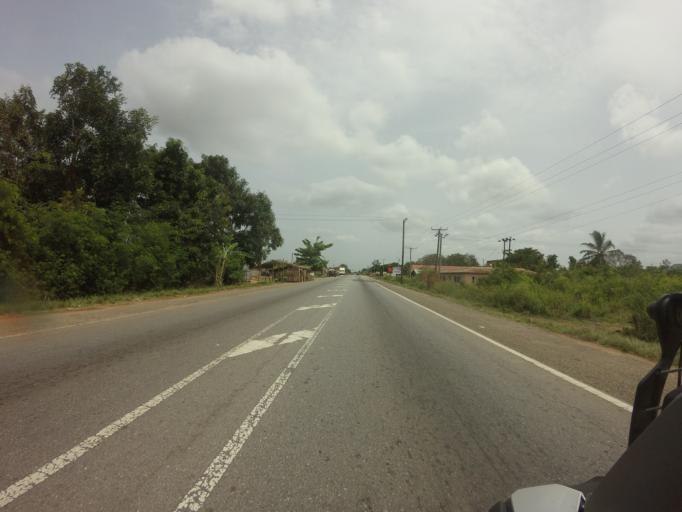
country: GH
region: Volta
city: Anloga
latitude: 5.9816
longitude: 0.5259
